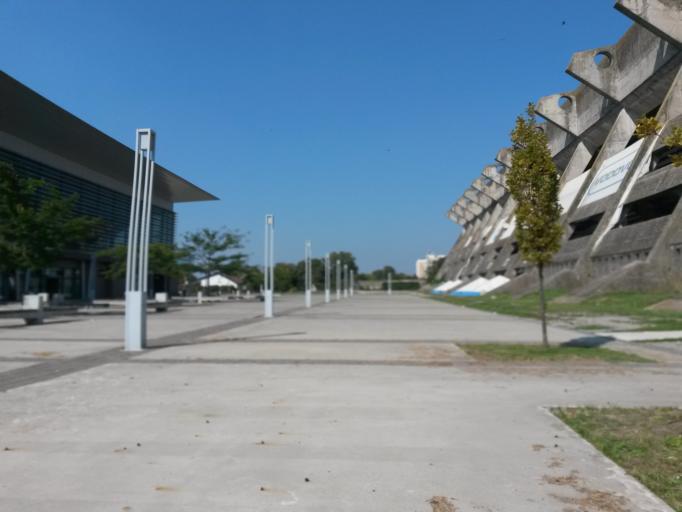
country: HR
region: Osjecko-Baranjska
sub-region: Grad Osijek
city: Osijek
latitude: 45.5440
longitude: 18.6943
